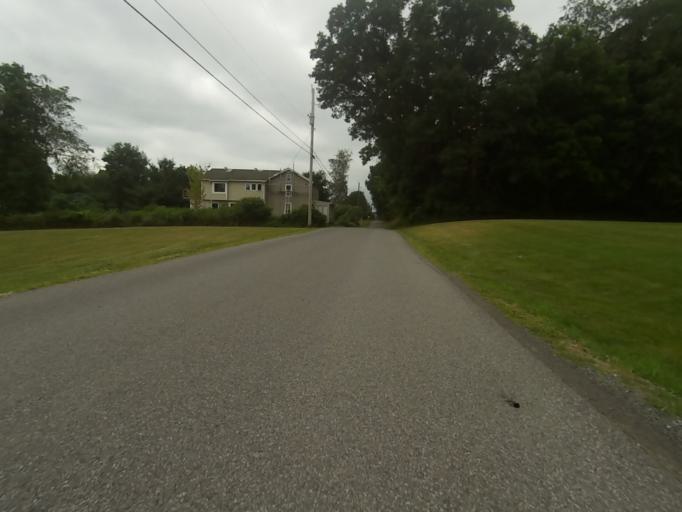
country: US
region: Pennsylvania
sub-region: Centre County
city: Stormstown
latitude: 40.7181
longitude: -78.0686
